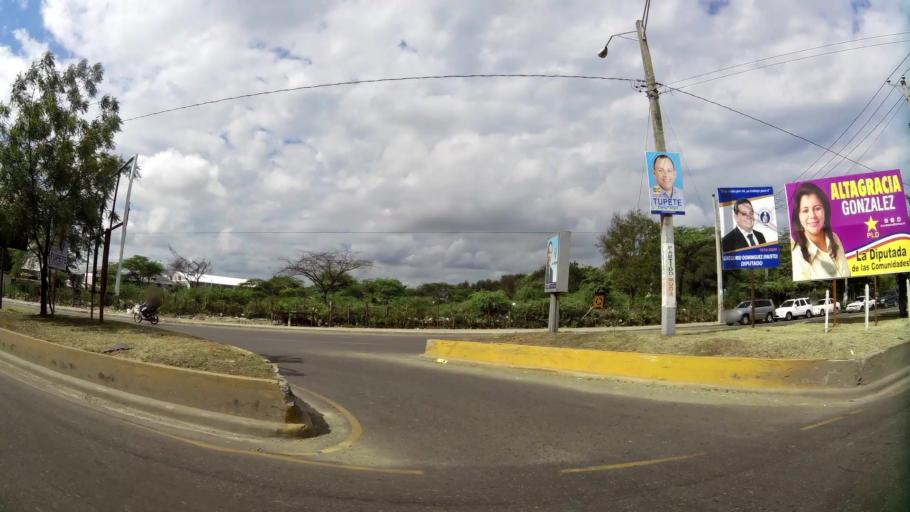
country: DO
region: Santiago
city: Santiago de los Caballeros
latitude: 19.4789
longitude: -70.7256
